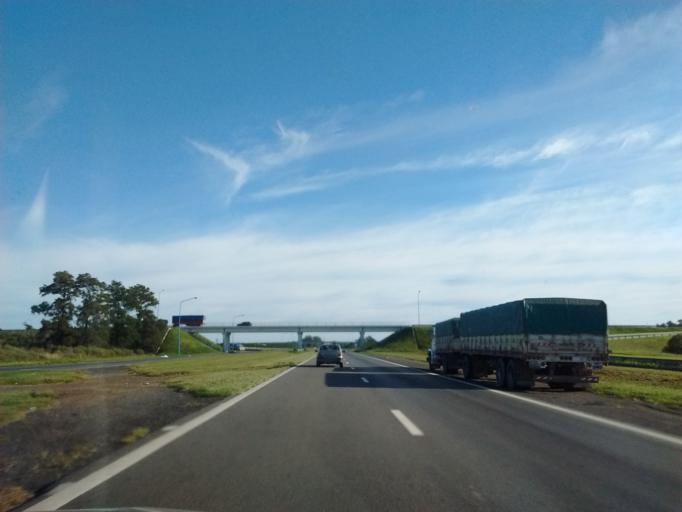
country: AR
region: Santa Fe
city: Totoras
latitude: -32.3648
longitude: -60.9530
